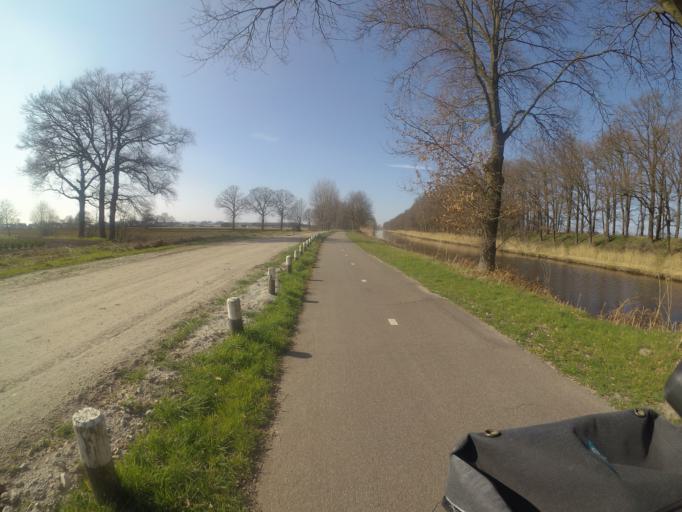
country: NL
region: North Brabant
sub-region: Gemeente Hilvarenbeek
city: Hilvarenbeek
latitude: 51.5120
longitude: 5.1600
